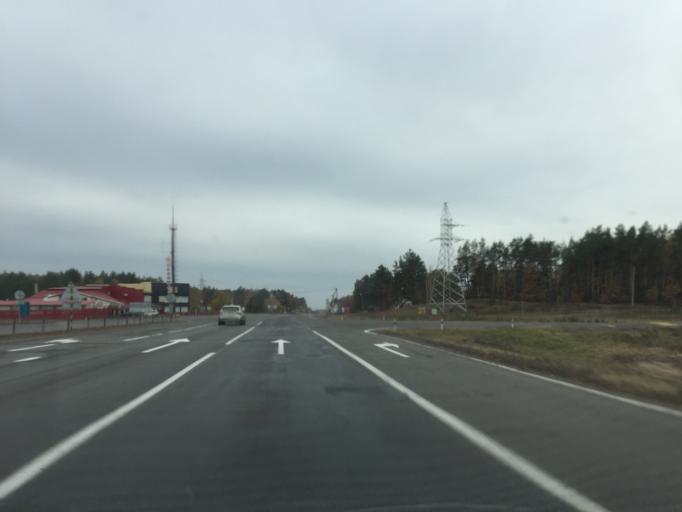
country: BY
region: Gomel
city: Horad Rechytsa
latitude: 52.3337
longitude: 30.5442
